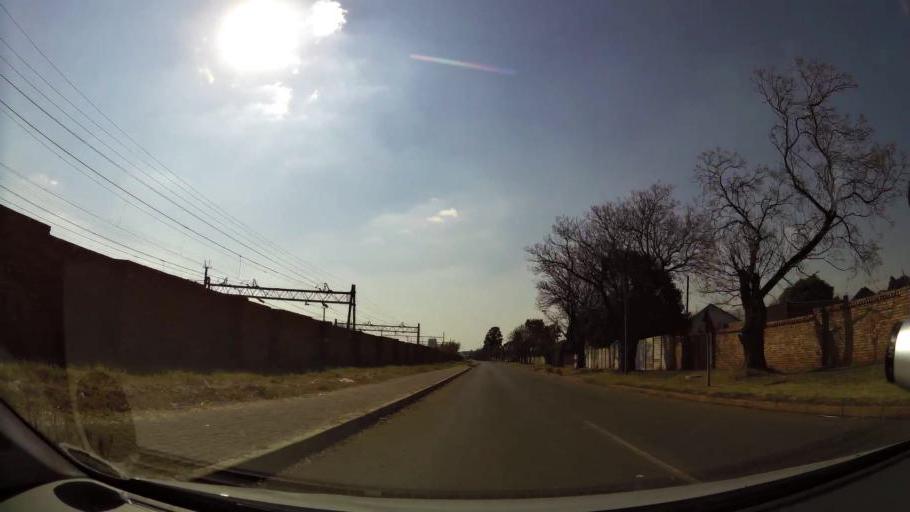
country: ZA
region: Gauteng
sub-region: City of Johannesburg Metropolitan Municipality
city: Modderfontein
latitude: -26.1235
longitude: 28.2261
